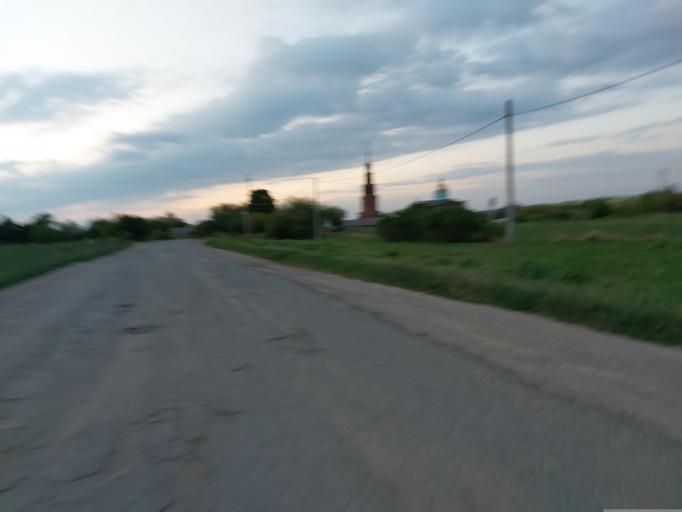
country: RU
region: Lipetsk
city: Dolgorukovo
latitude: 52.3747
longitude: 38.0526
